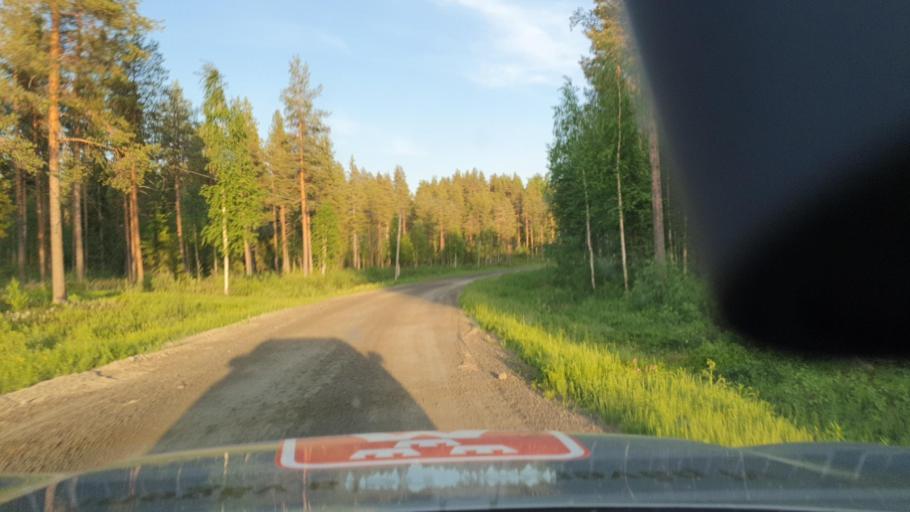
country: SE
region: Norrbotten
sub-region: Bodens Kommun
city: Boden
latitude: 66.1594
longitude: 21.5548
